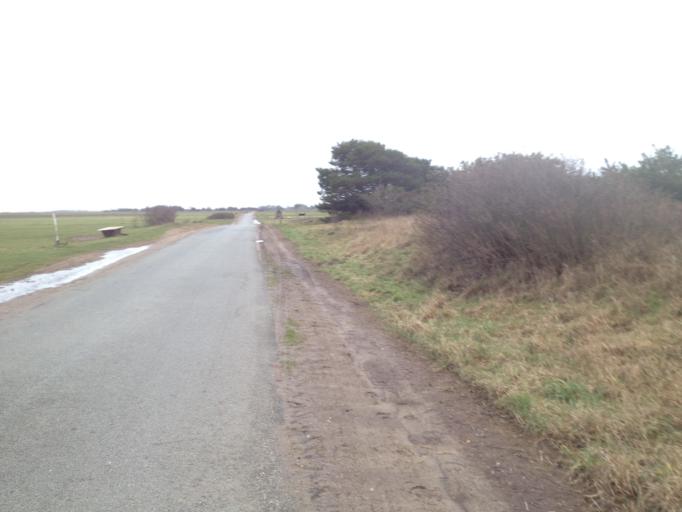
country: DE
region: Schleswig-Holstein
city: Nebel
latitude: 54.6655
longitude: 8.3452
